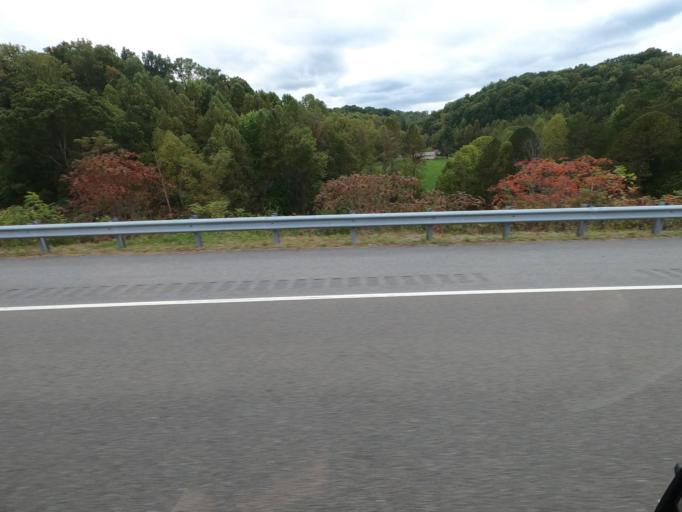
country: US
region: Tennessee
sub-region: Carter County
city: Central
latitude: 36.2822
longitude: -82.2408
